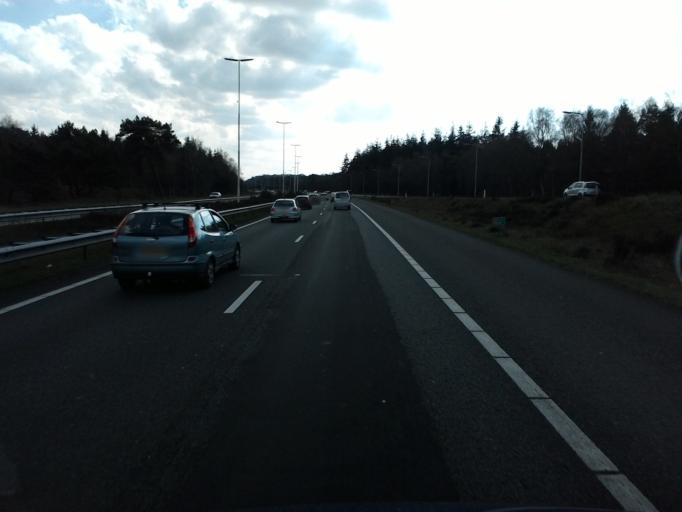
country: NL
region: North Holland
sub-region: Gemeente Hilversum
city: Hilversum
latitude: 52.1973
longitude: 5.1889
